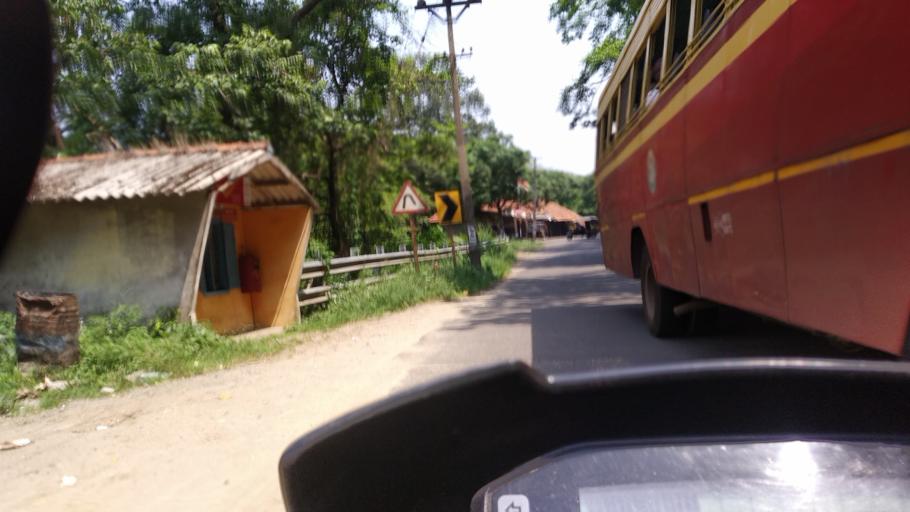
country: IN
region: Kerala
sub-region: Kottayam
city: Erattupetta
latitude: 9.6987
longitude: 76.8638
